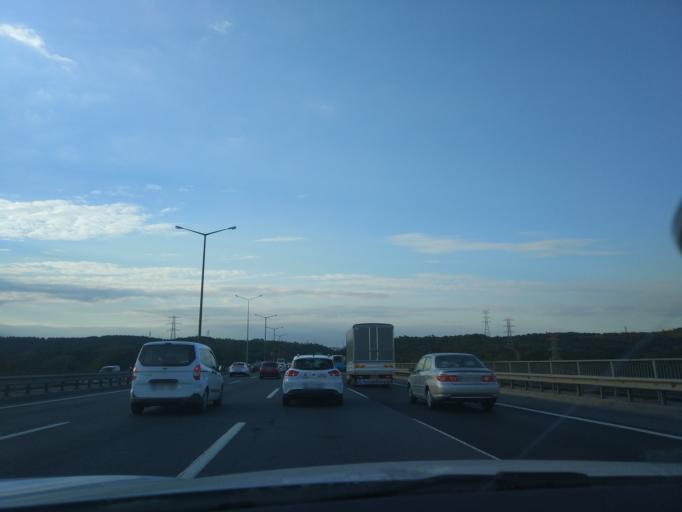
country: TR
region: Istanbul
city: Umraniye
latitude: 41.0741
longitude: 29.1024
